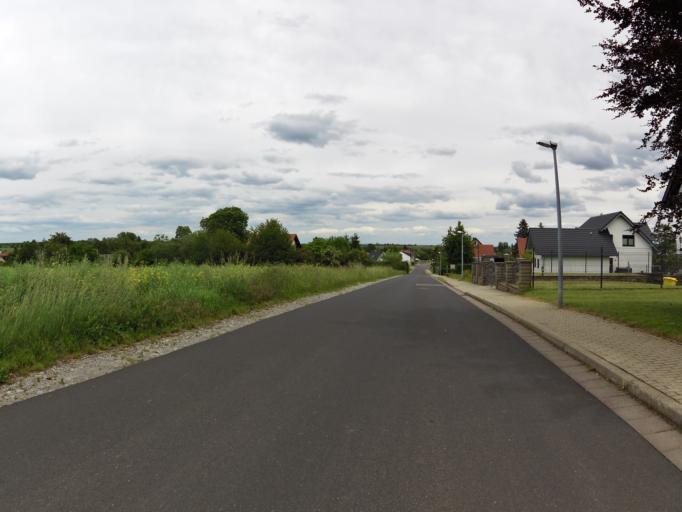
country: DE
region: Thuringia
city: Oberdorla
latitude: 51.1661
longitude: 10.4329
